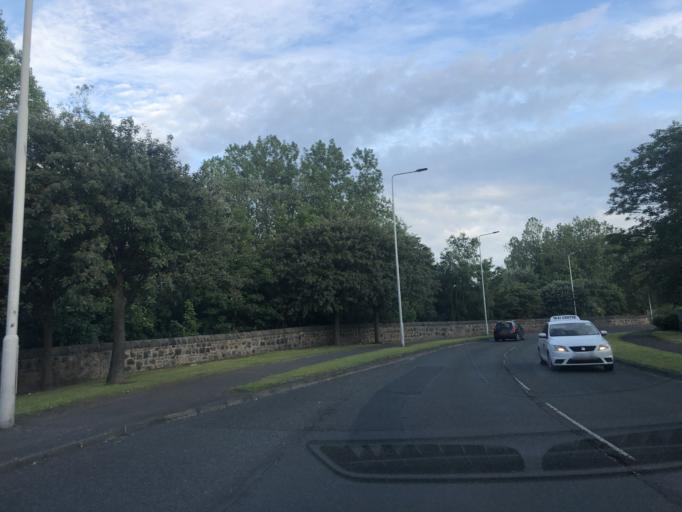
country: GB
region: Scotland
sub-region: Fife
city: Leven
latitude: 56.1913
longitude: -3.0017
